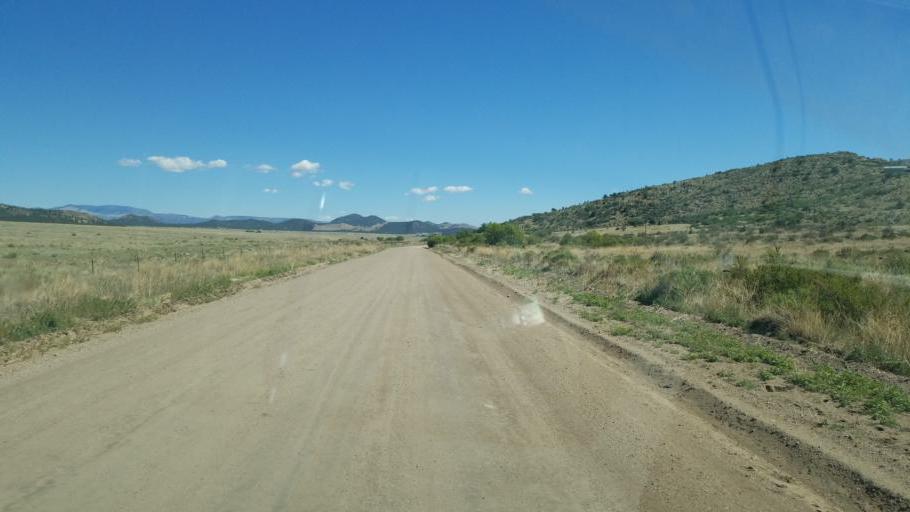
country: US
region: Colorado
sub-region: Custer County
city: Westcliffe
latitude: 38.2376
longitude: -105.5022
